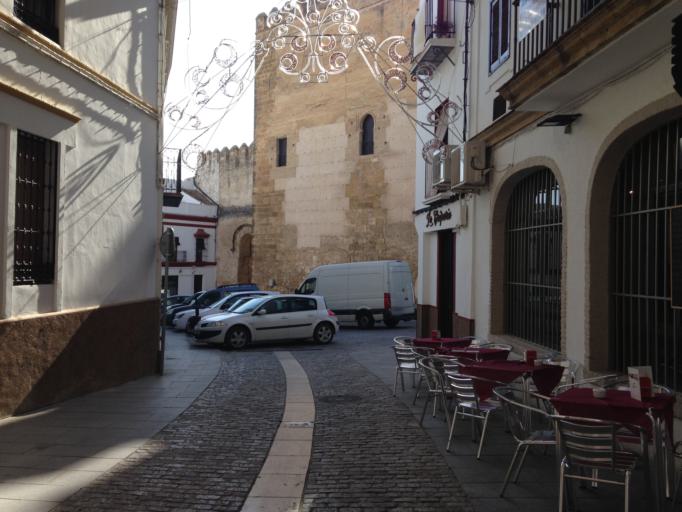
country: ES
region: Andalusia
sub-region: Provincia de Sevilla
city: Carmona
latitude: 37.4715
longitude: -5.6405
